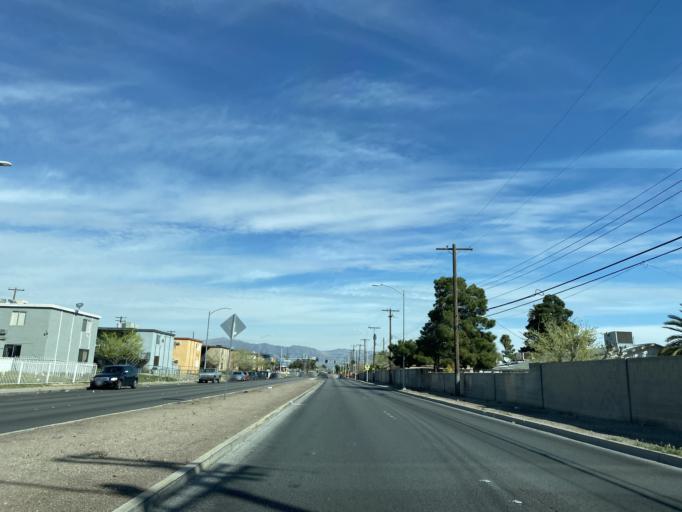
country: US
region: Nevada
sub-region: Clark County
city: Las Vegas
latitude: 36.1793
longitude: -115.1251
